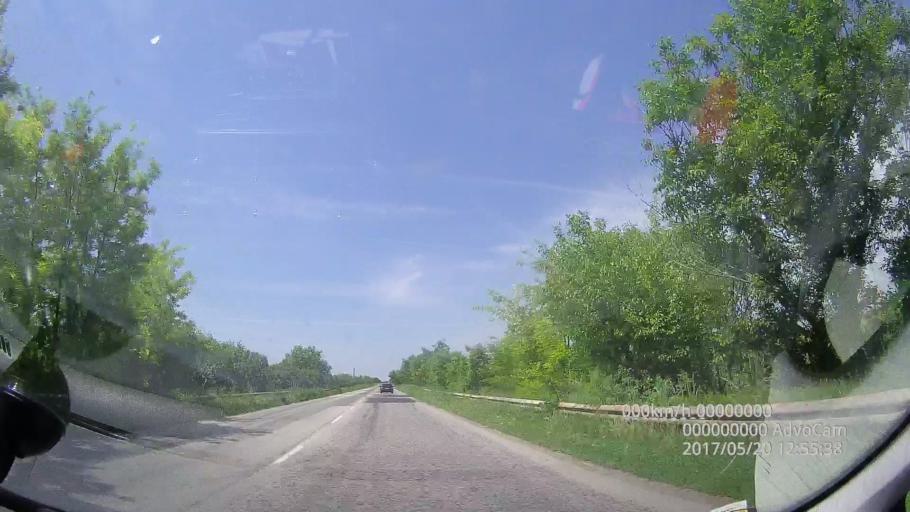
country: BG
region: Pleven
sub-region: Obshtina Dolna Mitropoliya
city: Dolna Mitropoliya
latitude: 43.4349
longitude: 24.5134
